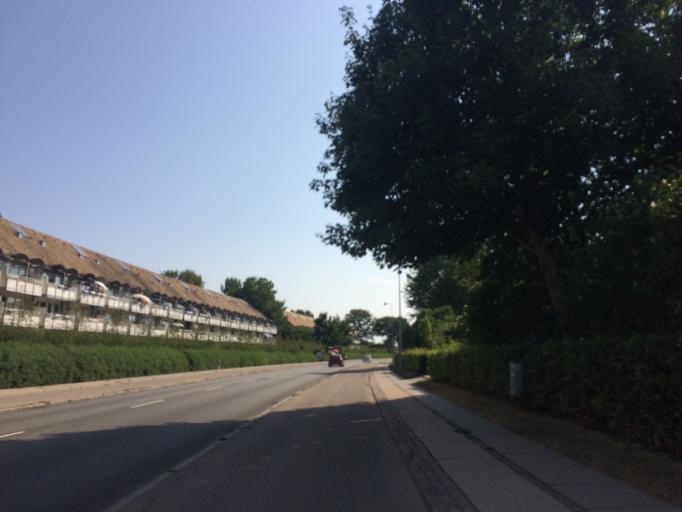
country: DK
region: Capital Region
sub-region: Hvidovre Kommune
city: Hvidovre
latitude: 55.6386
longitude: 12.4693
